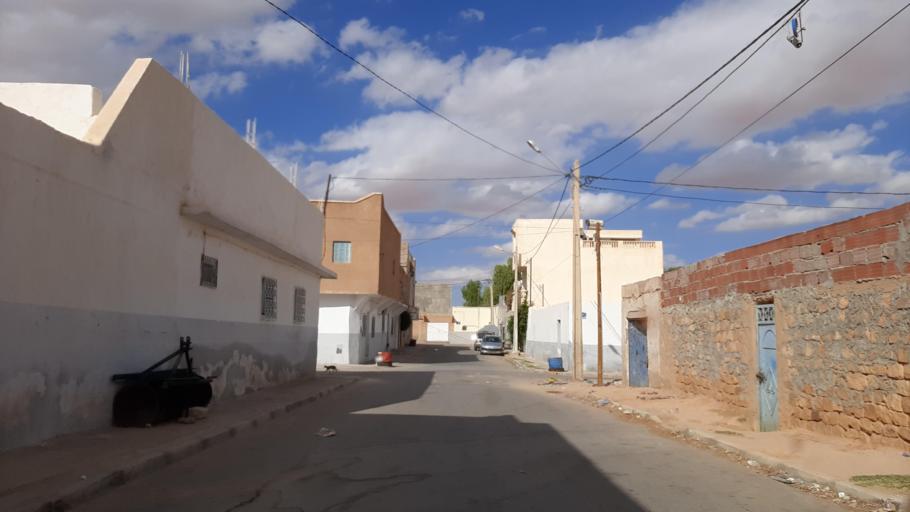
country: TN
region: Tataouine
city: Tataouine
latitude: 32.9272
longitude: 10.4571
